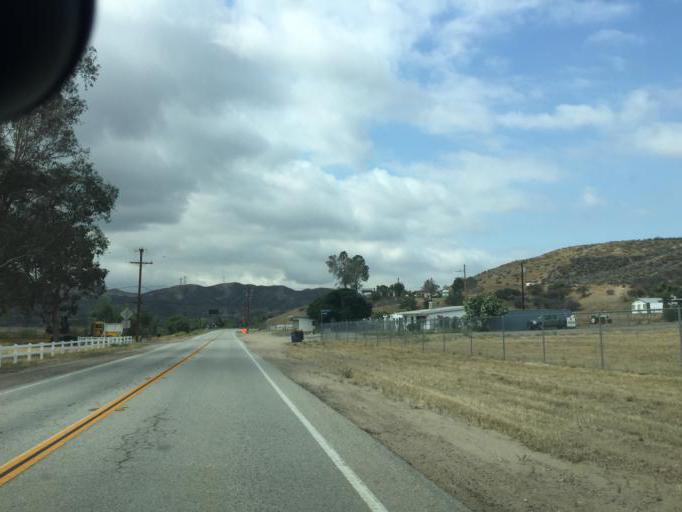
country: US
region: California
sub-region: Los Angeles County
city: Santa Clarita
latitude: 34.4784
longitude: -118.4658
